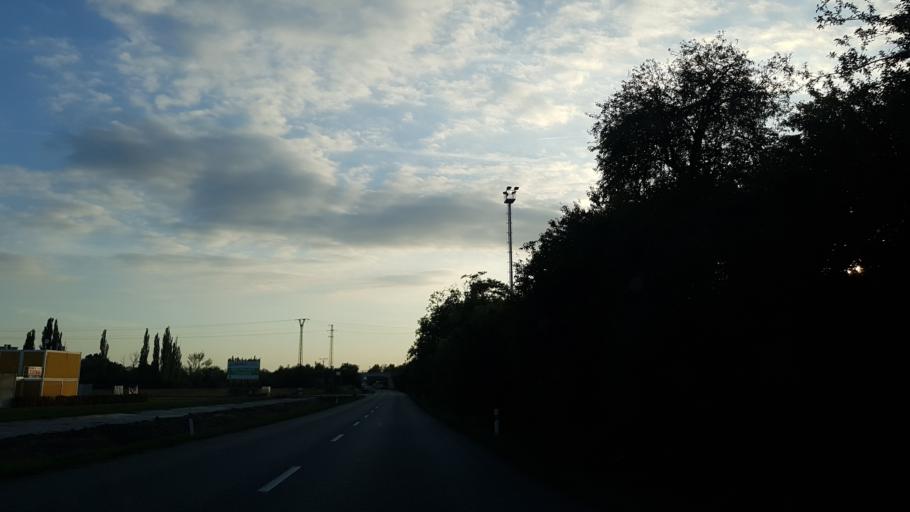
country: CZ
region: Zlin
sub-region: Okres Uherske Hradiste
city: Stare Mesto
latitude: 49.0704
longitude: 17.4173
